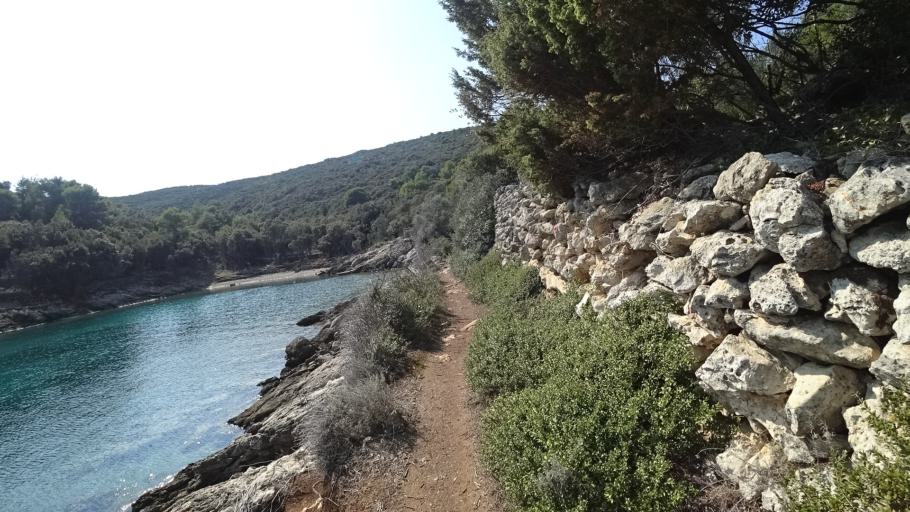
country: HR
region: Primorsko-Goranska
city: Mali Losinj
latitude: 44.5025
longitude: 14.5237
